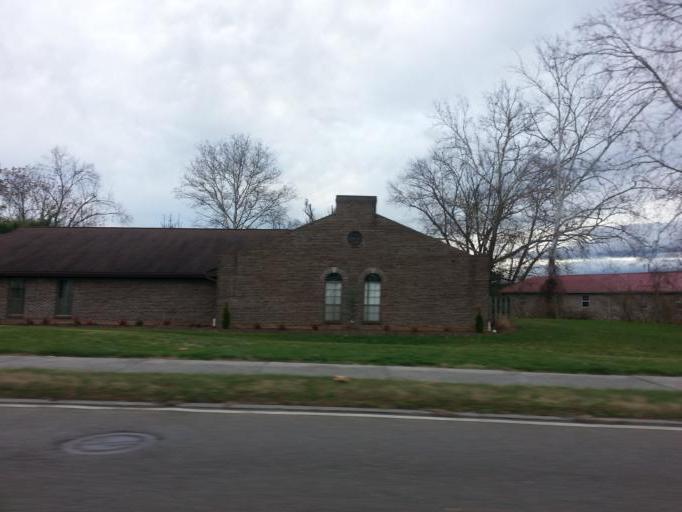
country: US
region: Tennessee
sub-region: Washington County
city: Johnson City
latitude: 36.3181
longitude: -82.3663
